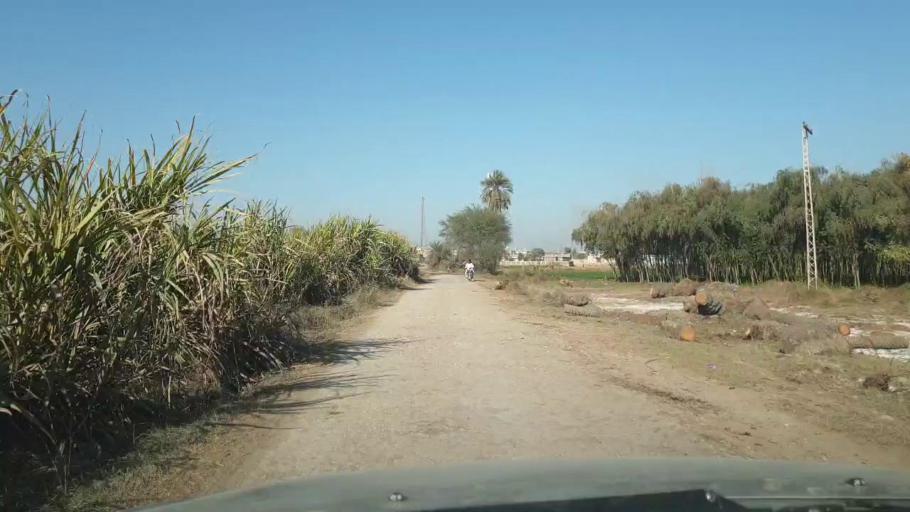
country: PK
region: Sindh
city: Ghotki
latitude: 28.0583
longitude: 69.3377
